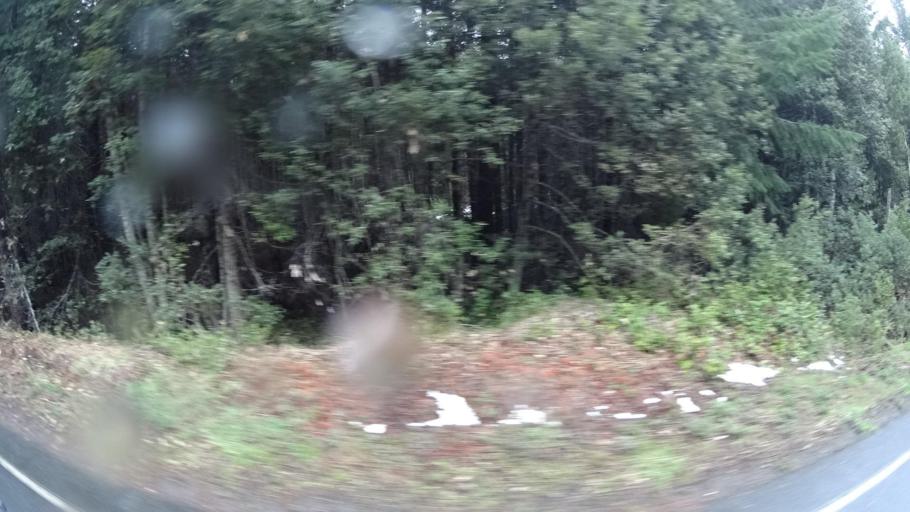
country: US
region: California
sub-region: Humboldt County
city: Willow Creek
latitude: 41.1701
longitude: -123.8140
